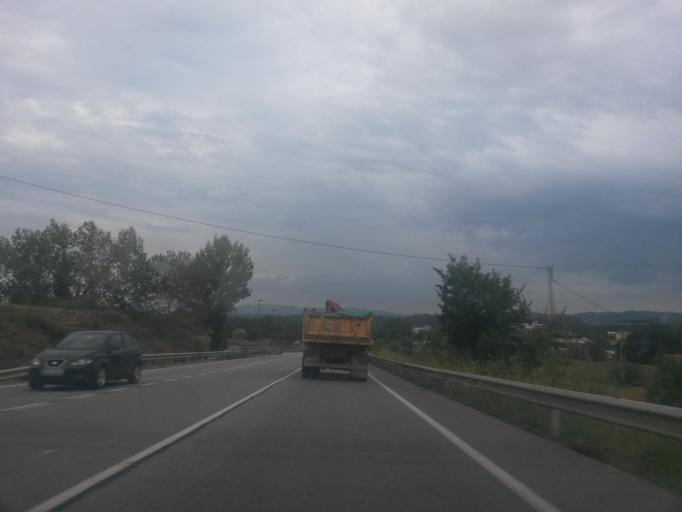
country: ES
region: Catalonia
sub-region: Provincia de Girona
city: Fontcoberta
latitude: 42.1050
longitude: 2.7952
